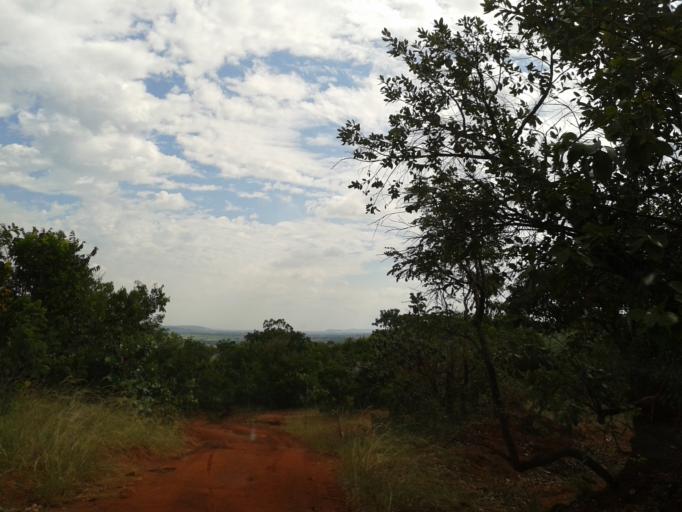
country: BR
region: Minas Gerais
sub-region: Campina Verde
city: Campina Verde
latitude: -19.3931
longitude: -49.6610
